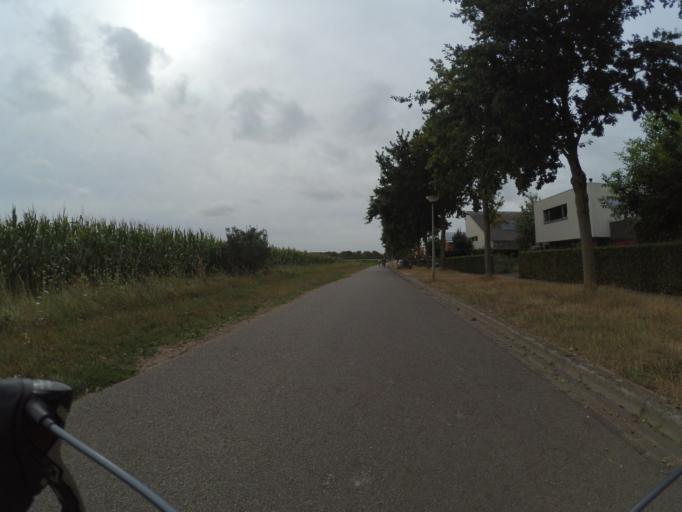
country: NL
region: Limburg
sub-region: Gemeente Maastricht
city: Heer
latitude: 50.8592
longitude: 5.7389
